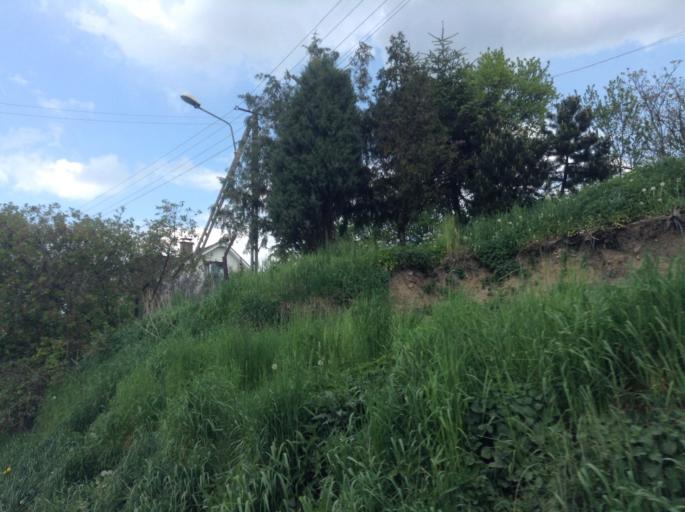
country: PL
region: Warmian-Masurian Voivodeship
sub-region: Powiat ilawski
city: Ilawa
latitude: 53.5143
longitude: 19.5680
